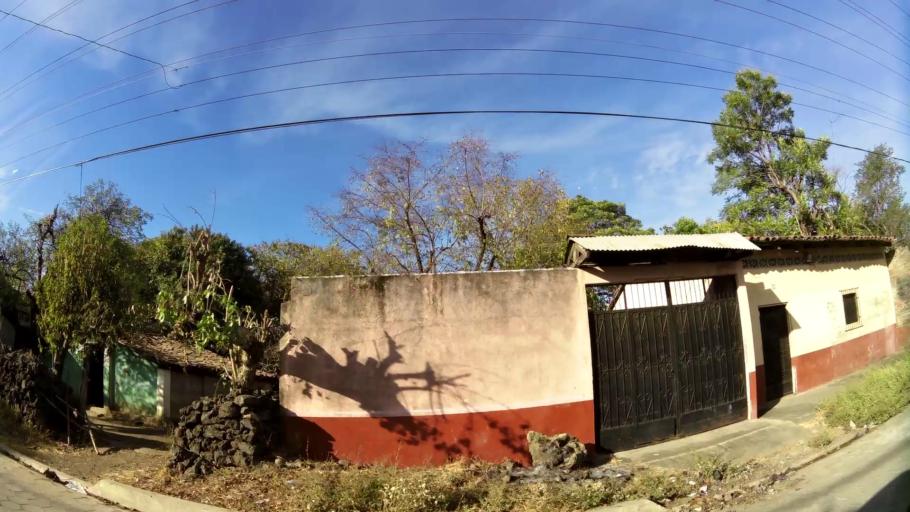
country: SV
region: San Miguel
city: San Miguel
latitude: 13.4621
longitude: -88.1824
